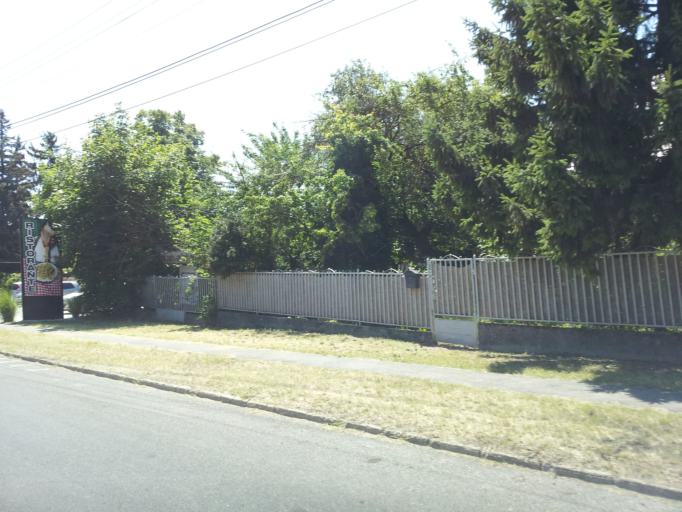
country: HU
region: Veszprem
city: Balatonkenese
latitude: 47.0190
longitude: 18.1570
